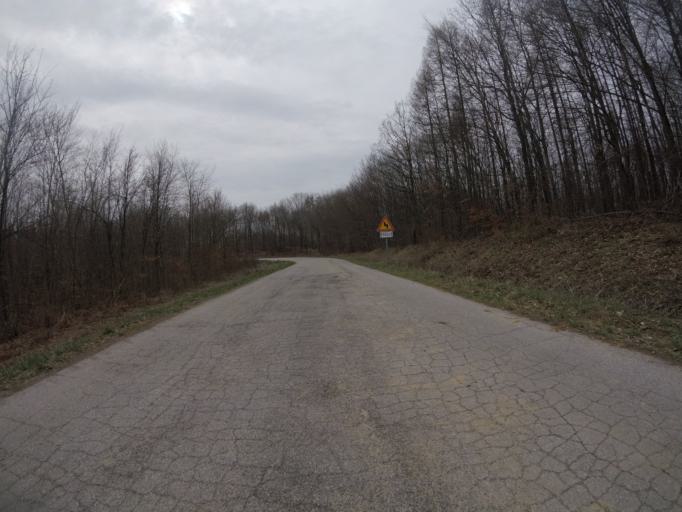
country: HR
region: Zagrebacka
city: Lukavec
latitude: 45.5866
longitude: 15.9625
